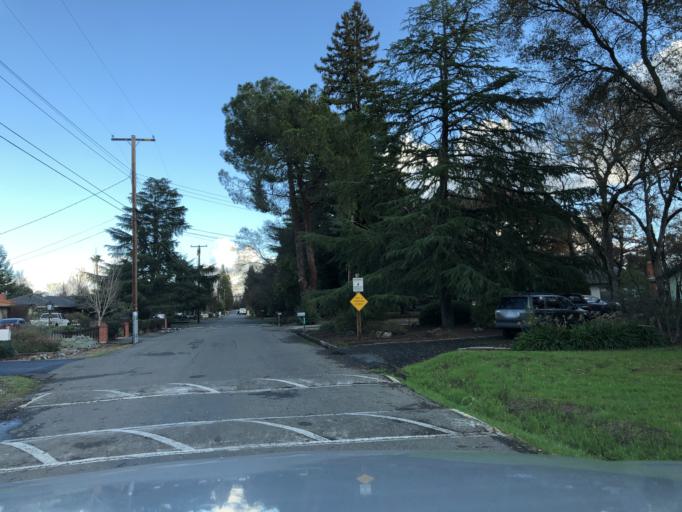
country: US
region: California
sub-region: Sacramento County
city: Foothill Farms
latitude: 38.6560
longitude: -121.3265
